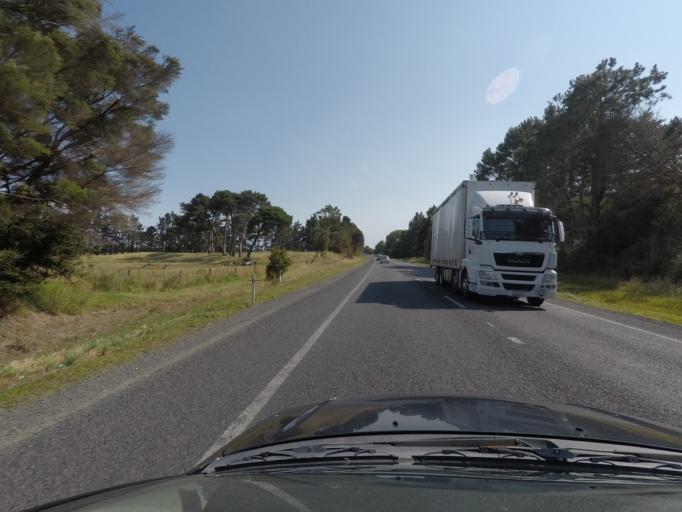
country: NZ
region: Northland
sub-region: Whangarei
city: Ruakaka
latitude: -35.9582
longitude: 174.4502
